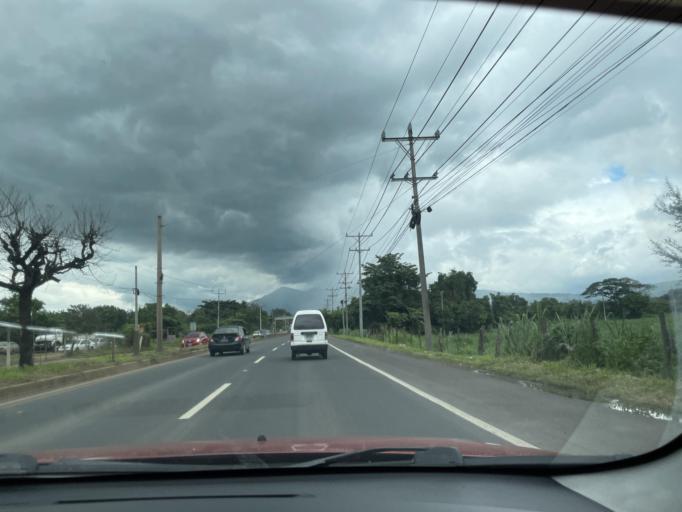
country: SV
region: Sonsonate
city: Armenia
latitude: 13.7401
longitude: -89.4214
